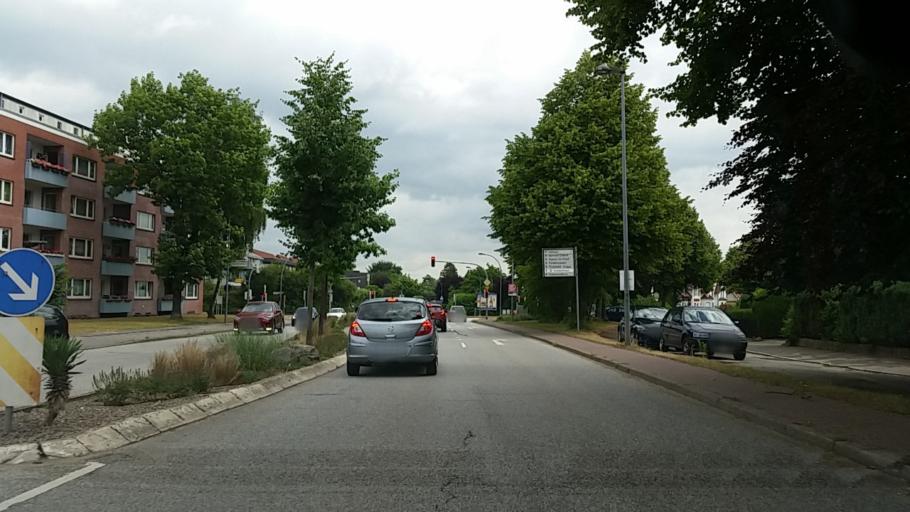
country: DE
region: Schleswig-Holstein
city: Bad Oldesloe
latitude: 53.8029
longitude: 10.3595
